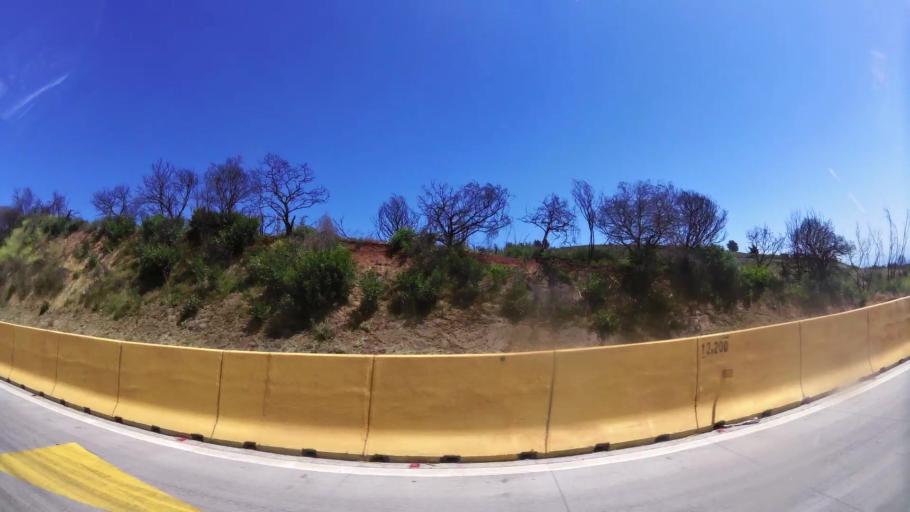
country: CL
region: Valparaiso
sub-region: Provincia de Valparaiso
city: Valparaiso
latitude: -33.0587
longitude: -71.6467
